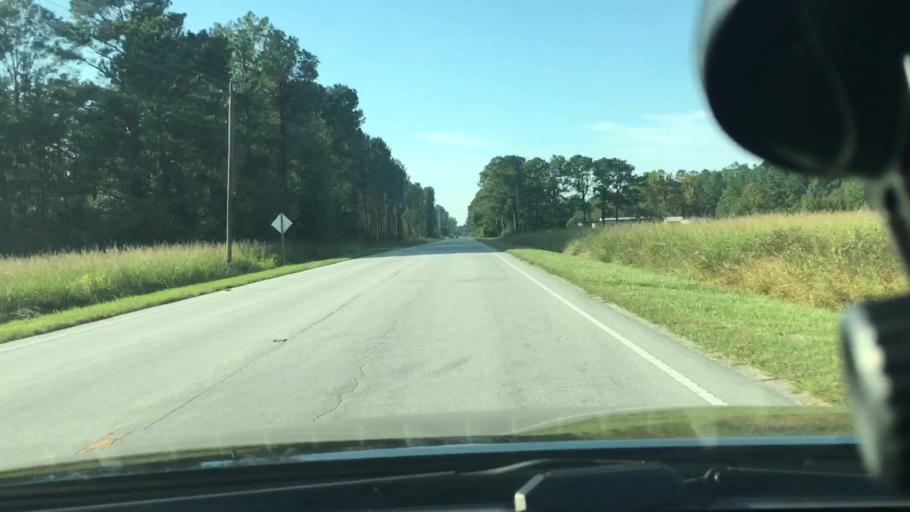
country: US
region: North Carolina
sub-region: Craven County
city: Vanceboro
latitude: 35.3423
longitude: -77.1792
